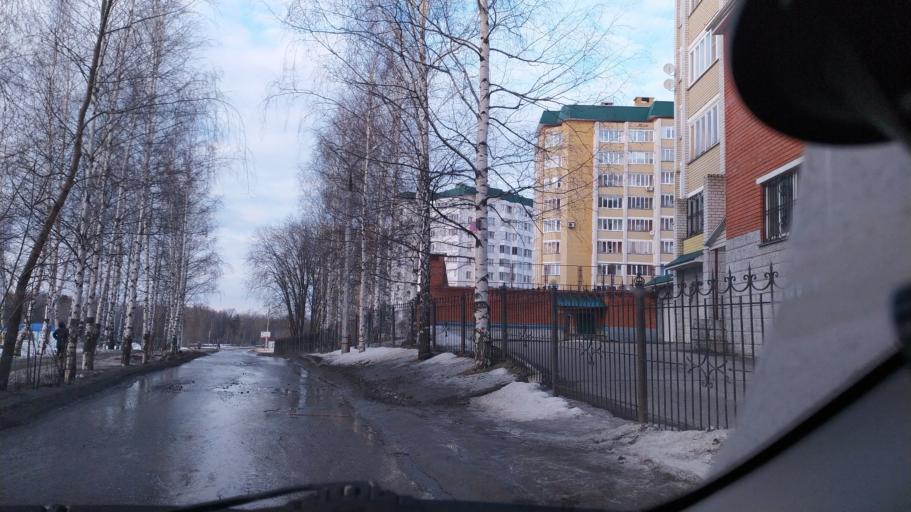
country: RU
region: Chuvashia
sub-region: Cheboksarskiy Rayon
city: Cheboksary
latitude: 56.1474
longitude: 47.2145
